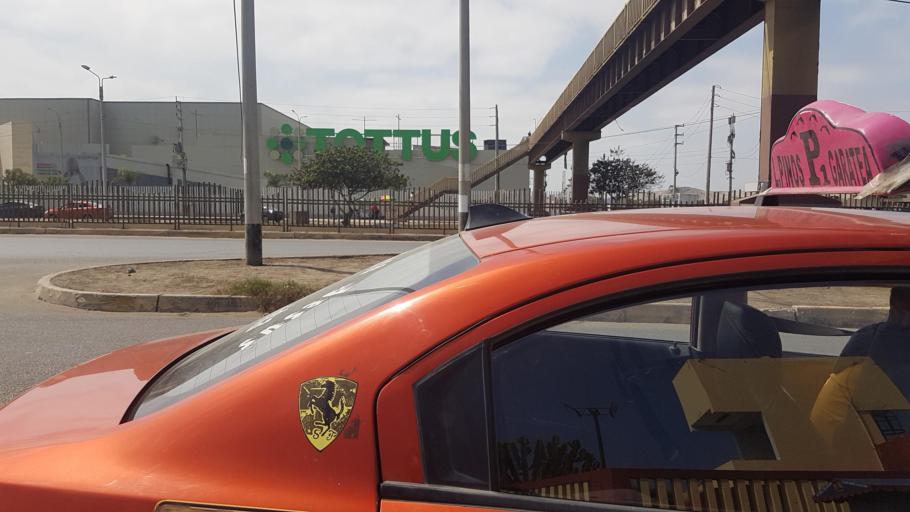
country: PE
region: Ancash
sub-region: Provincia de Santa
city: Chimbote
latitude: -9.1042
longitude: -78.5578
